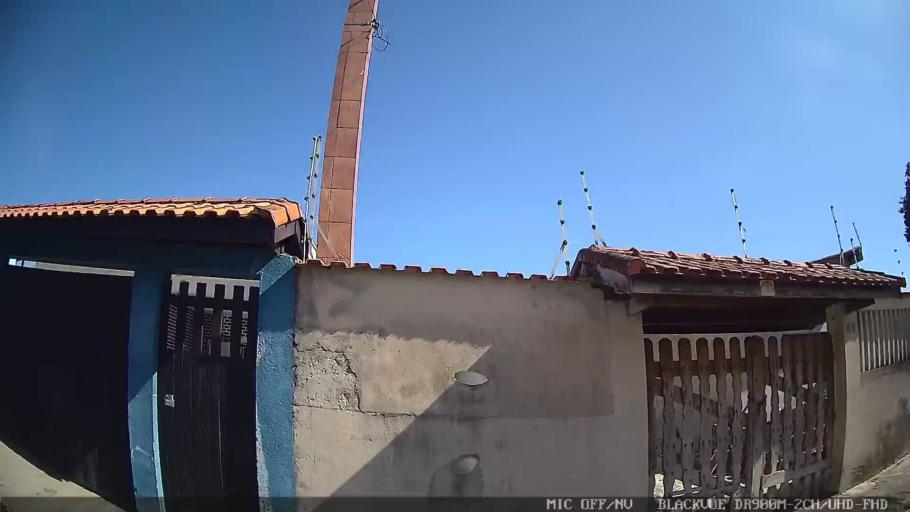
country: BR
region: Sao Paulo
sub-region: Peruibe
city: Peruibe
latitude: -24.2758
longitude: -46.9465
